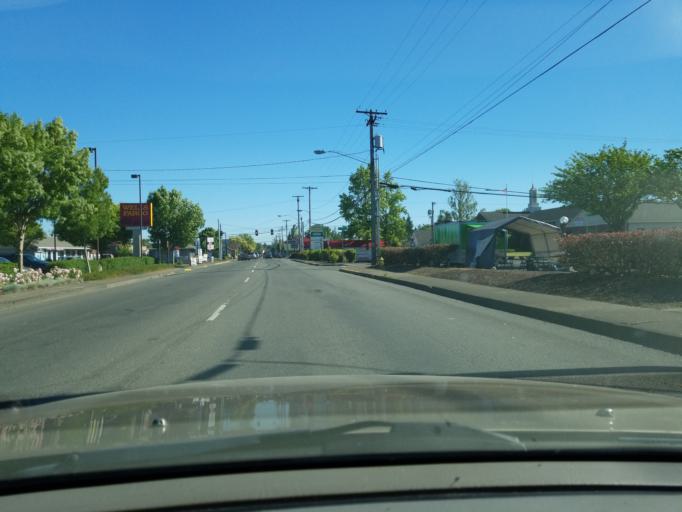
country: US
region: Oregon
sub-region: Yamhill County
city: McMinnville
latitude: 45.2176
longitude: -123.1990
